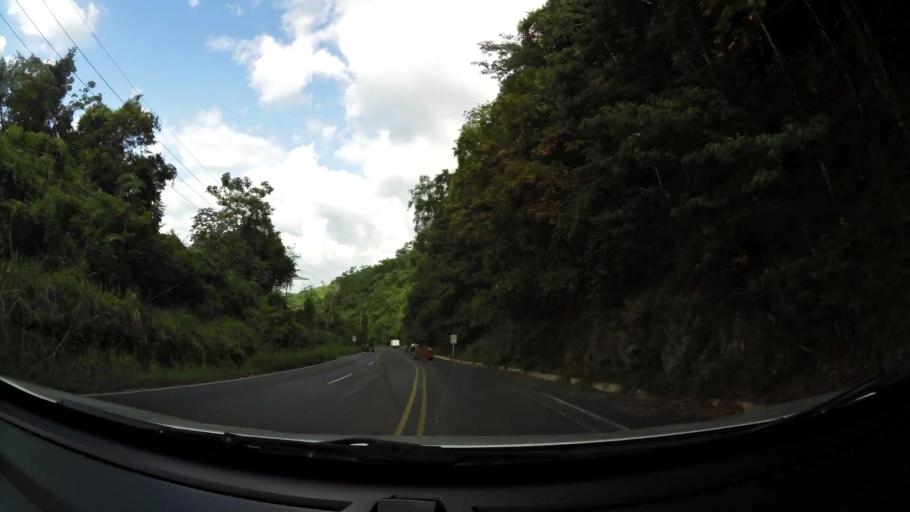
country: CR
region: Puntarenas
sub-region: Canton de Garabito
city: Jaco
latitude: 9.6919
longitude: -84.6425
